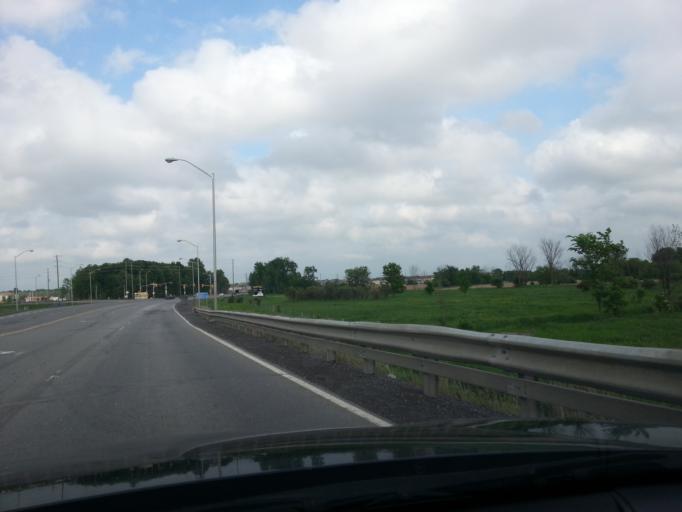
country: CA
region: Ontario
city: Bells Corners
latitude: 45.2719
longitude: -75.7904
